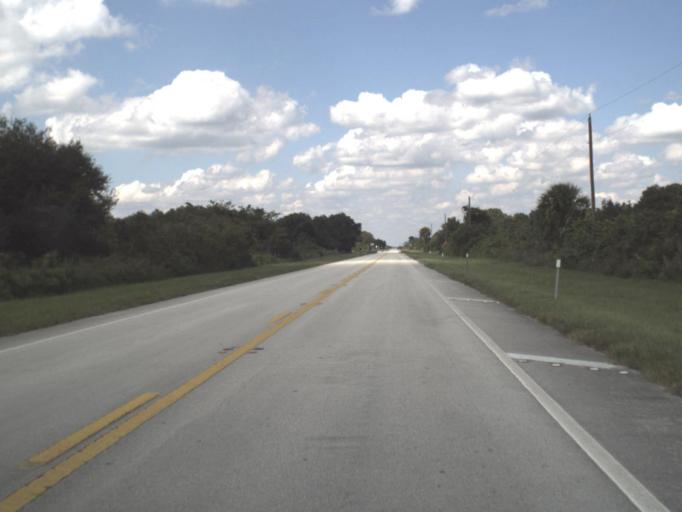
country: US
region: Florida
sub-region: Highlands County
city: Lake Placid
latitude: 27.3978
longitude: -81.1595
